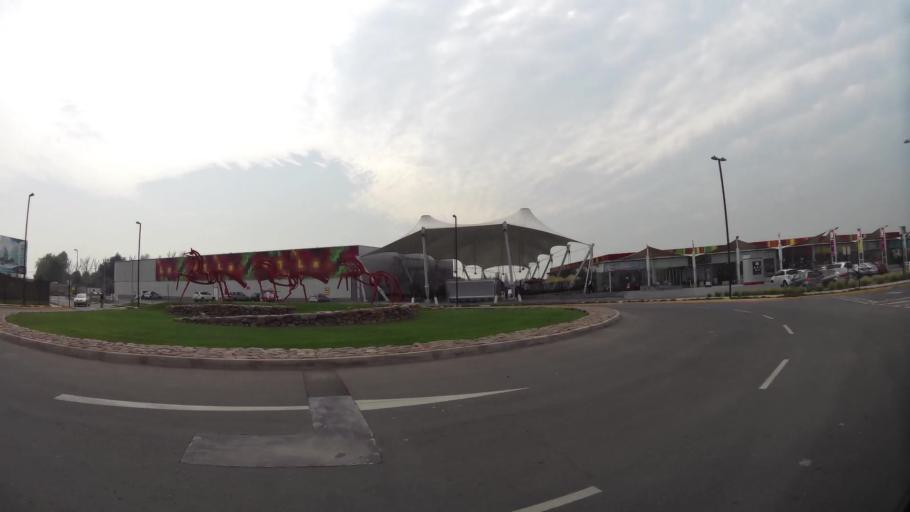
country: CL
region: Santiago Metropolitan
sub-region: Provincia de Chacabuco
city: Chicureo Abajo
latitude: -33.2866
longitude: -70.6992
